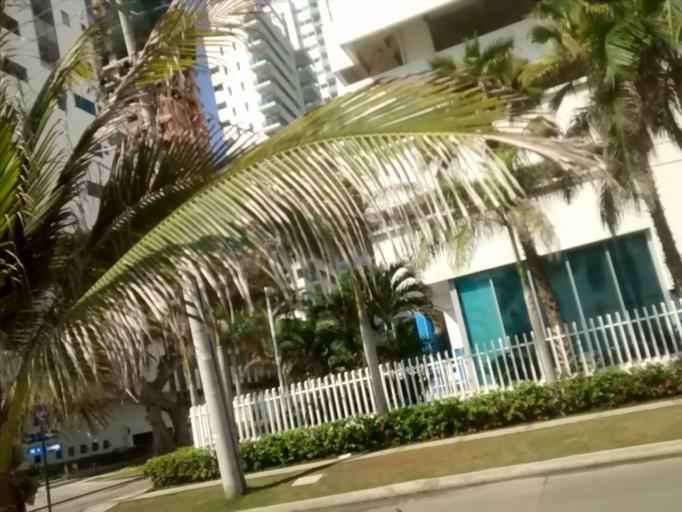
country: CO
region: Bolivar
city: Cartagena
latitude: 10.3948
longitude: -75.5499
